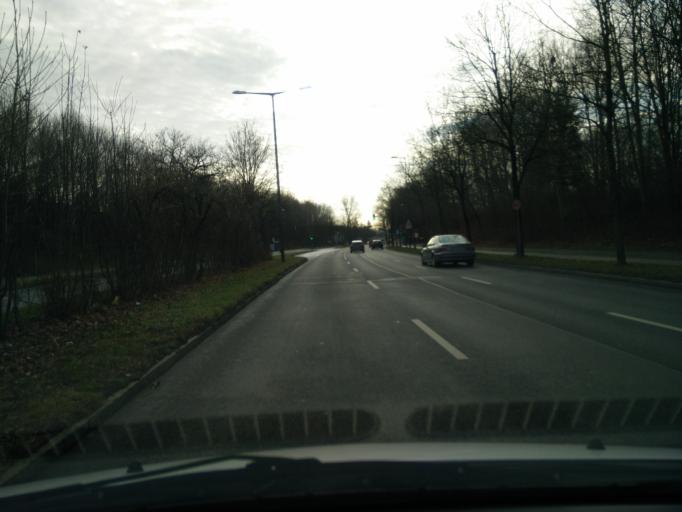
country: DE
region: Bavaria
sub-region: Upper Bavaria
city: Pasing
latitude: 48.1685
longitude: 11.5101
